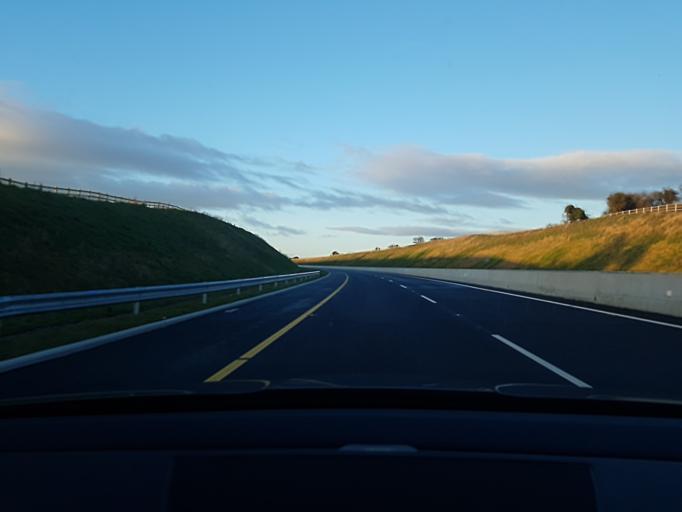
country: IE
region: Connaught
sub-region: County Galway
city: Athenry
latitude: 53.3633
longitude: -8.7882
